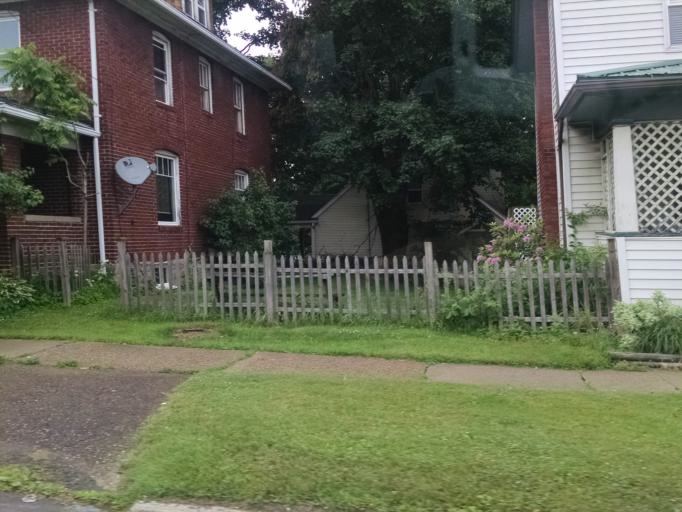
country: US
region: Pennsylvania
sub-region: Indiana County
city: Indiana
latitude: 40.6248
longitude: -79.1457
